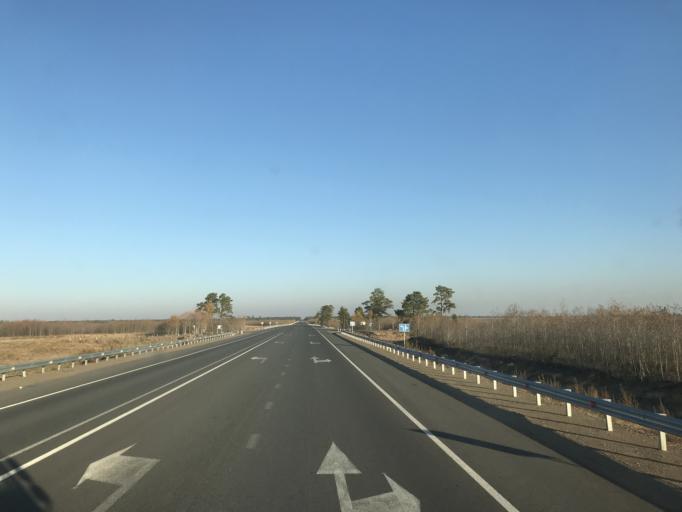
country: KZ
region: Pavlodar
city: Kurchatov
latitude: 51.1031
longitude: 78.9940
